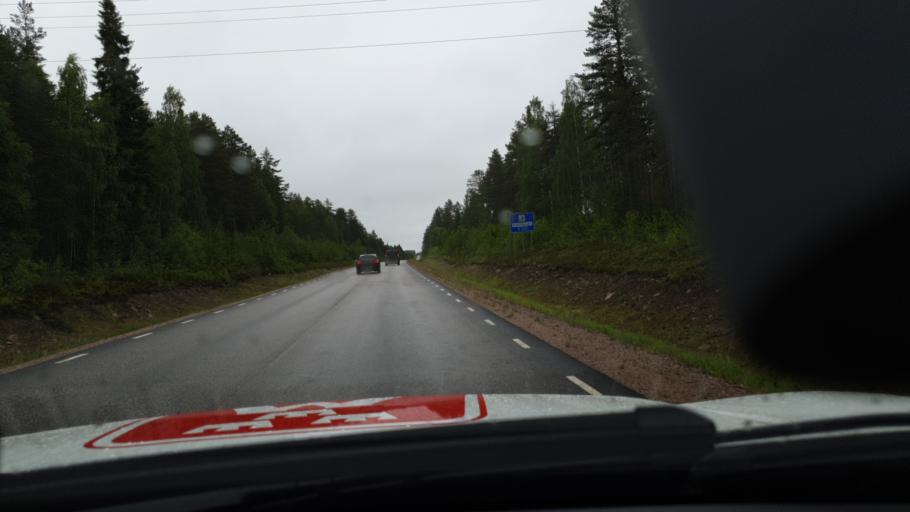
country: SE
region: Norrbotten
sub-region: Overtornea Kommun
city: OEvertornea
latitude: 66.5131
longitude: 23.7360
